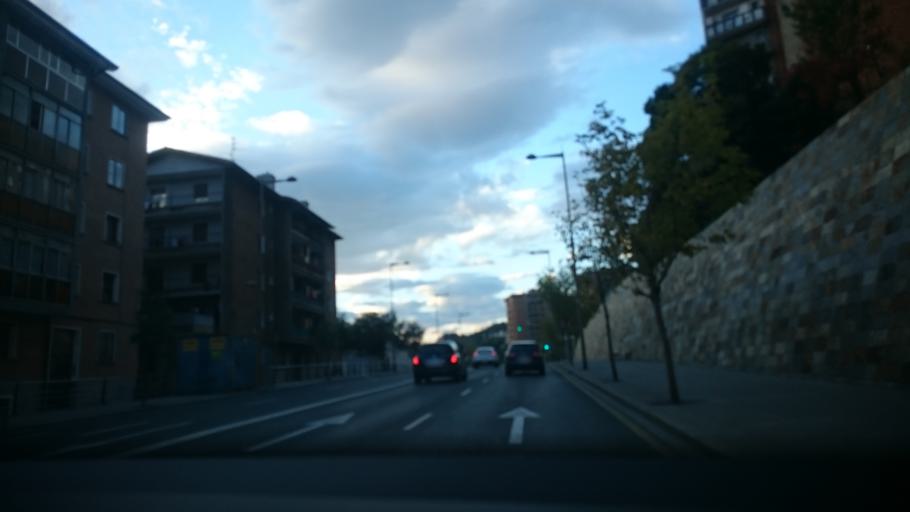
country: ES
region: Basque Country
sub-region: Bizkaia
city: Bilbao
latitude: 43.2684
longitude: -2.9195
